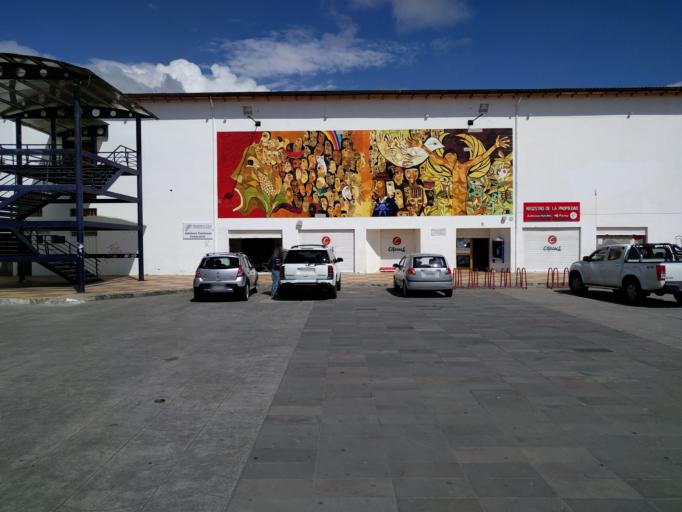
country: EC
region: Imbabura
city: Cotacachi
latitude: 0.2994
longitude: -78.2662
